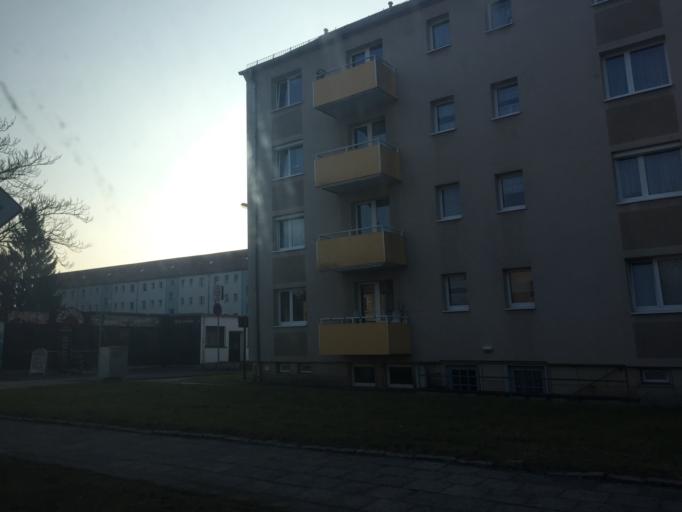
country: DE
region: Saxony
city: Pirna
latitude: 50.9727
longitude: 13.9314
